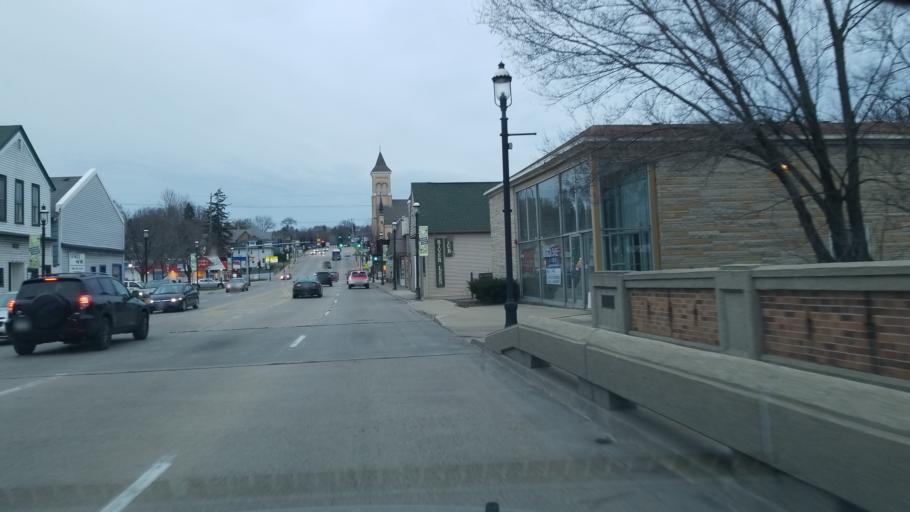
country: US
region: Illinois
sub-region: Kane County
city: East Dundee
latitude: 42.0981
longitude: -88.2759
